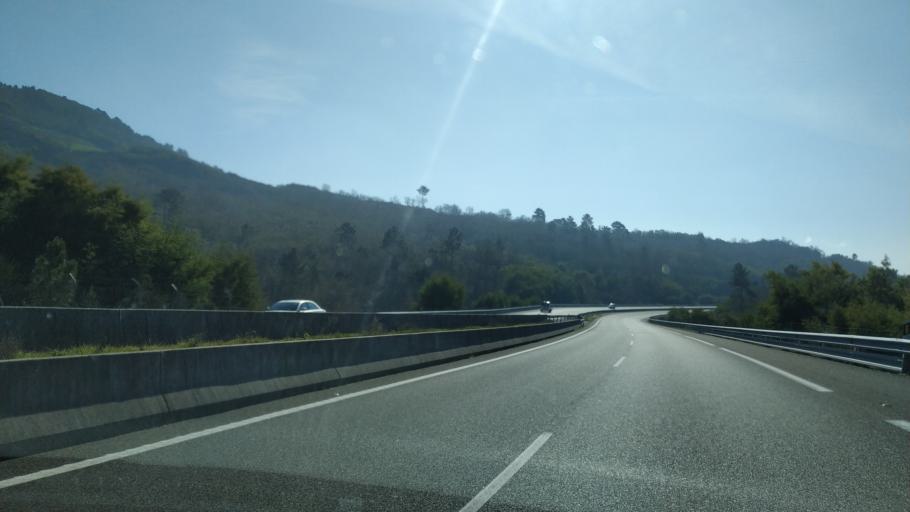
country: ES
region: Galicia
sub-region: Provincia de Ourense
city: Punxin
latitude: 42.3620
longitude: -7.9969
